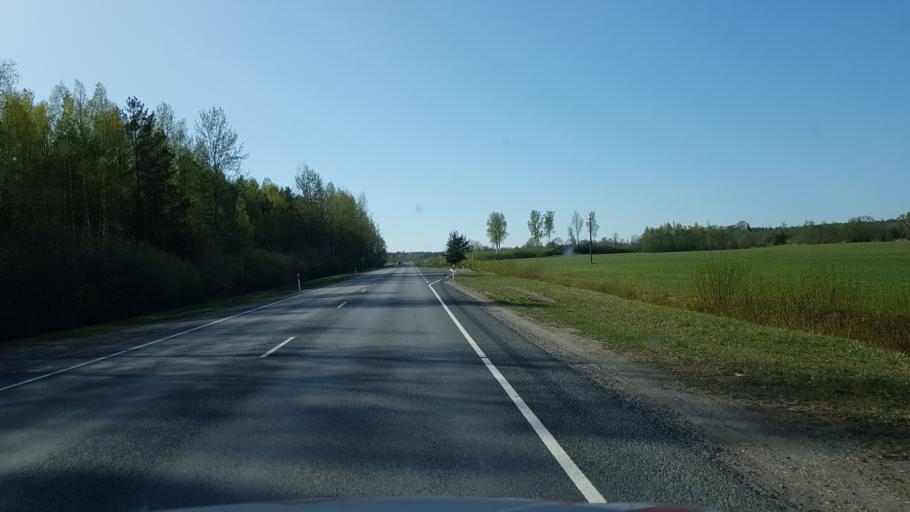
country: EE
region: Paernumaa
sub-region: Paikuse vald
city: Paikuse
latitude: 58.1967
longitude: 24.7461
